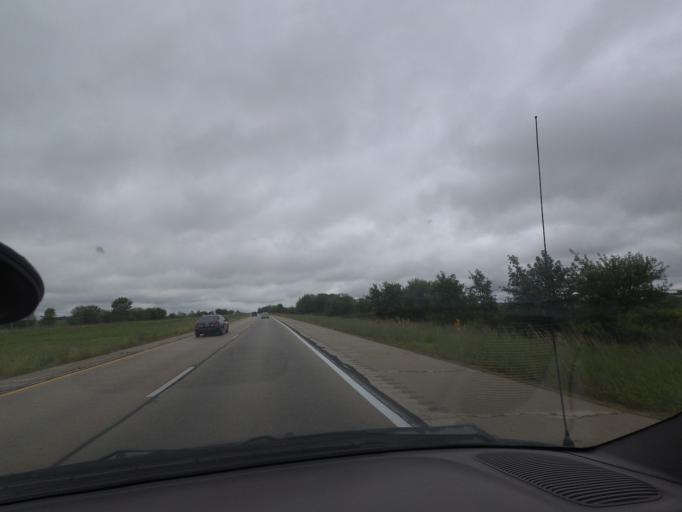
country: US
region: Illinois
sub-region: Piatt County
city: Cerro Gordo
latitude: 40.0186
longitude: -88.7192
